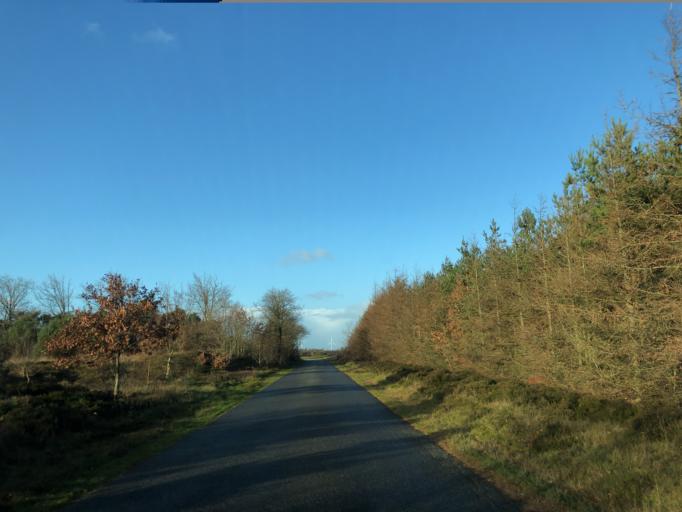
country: DK
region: Central Jutland
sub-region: Holstebro Kommune
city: Ulfborg
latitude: 56.2101
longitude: 8.2893
